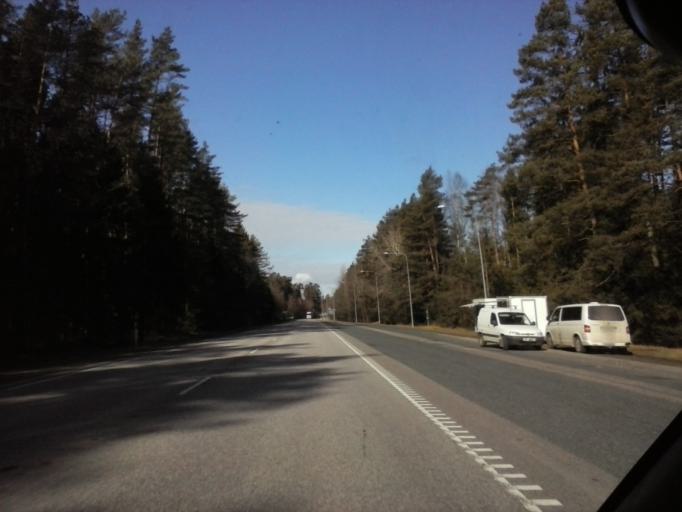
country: EE
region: Harju
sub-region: Raasiku vald
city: Raasiku
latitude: 59.1645
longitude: 25.1874
